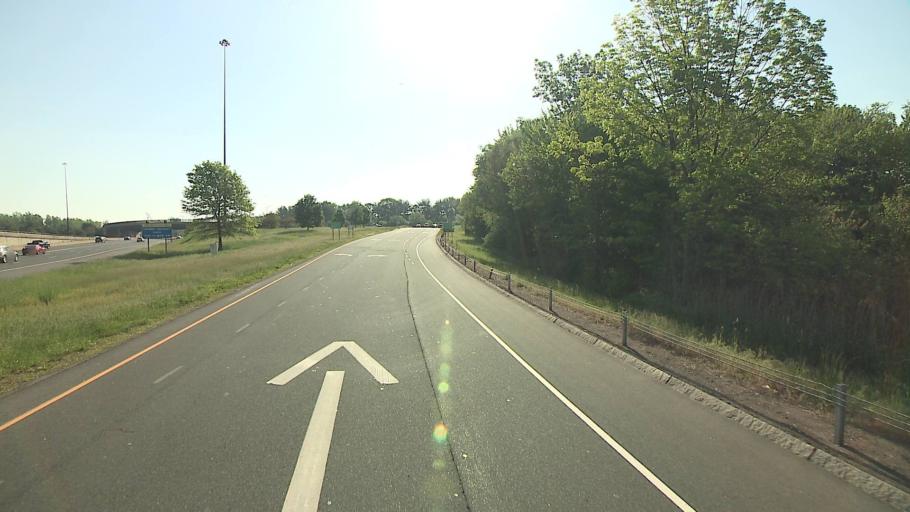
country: US
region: Connecticut
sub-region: Hartford County
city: East Hartford
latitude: 41.7639
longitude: -72.6293
